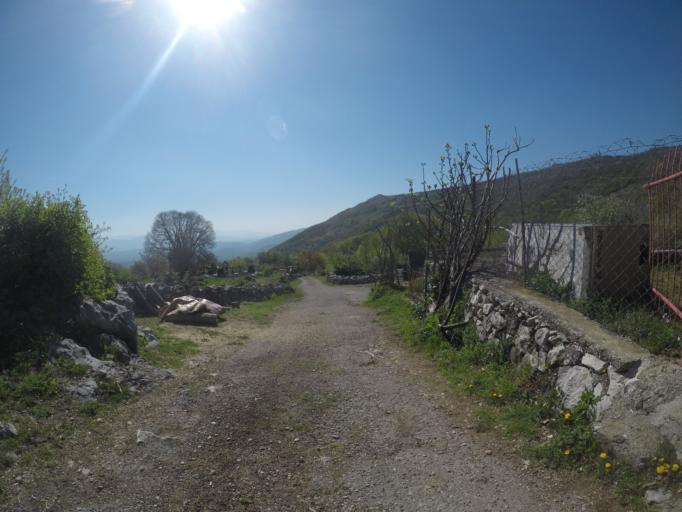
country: ME
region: Danilovgrad
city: Danilovgrad
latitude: 42.5178
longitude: 19.0549
